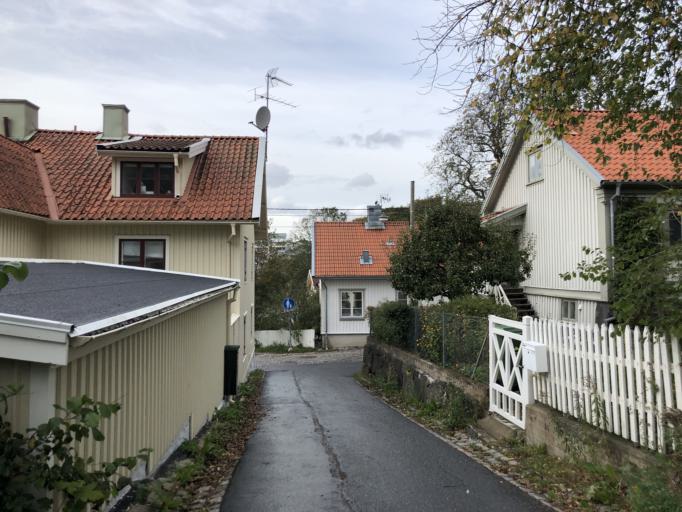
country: SE
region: Vaestra Goetaland
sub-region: Molndal
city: Moelndal
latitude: 57.6558
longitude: 12.0305
